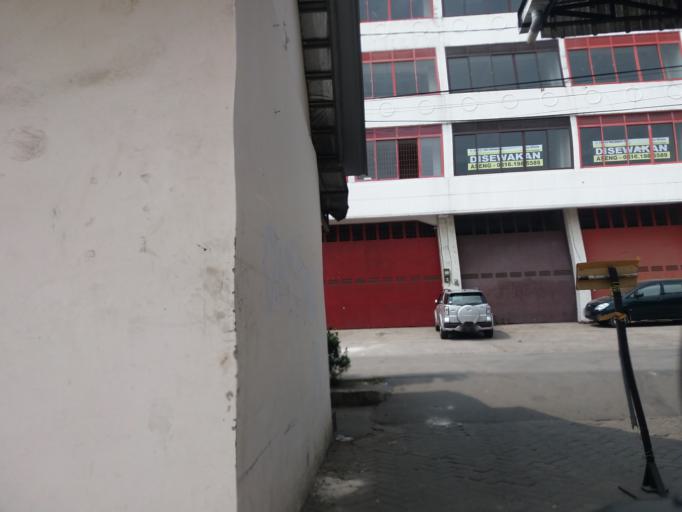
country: ID
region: Jakarta Raya
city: Jakarta
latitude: -6.1314
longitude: 106.8141
